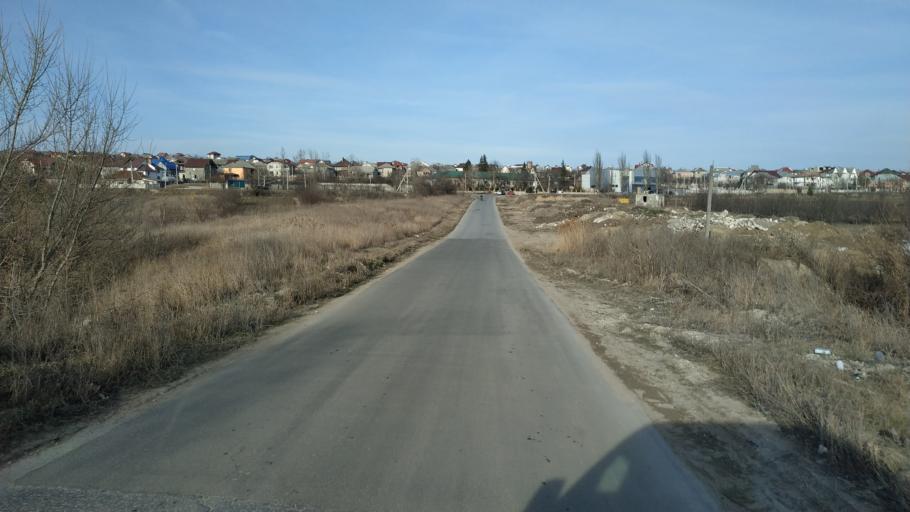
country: MD
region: Chisinau
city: Vatra
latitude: 47.0703
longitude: 28.6959
